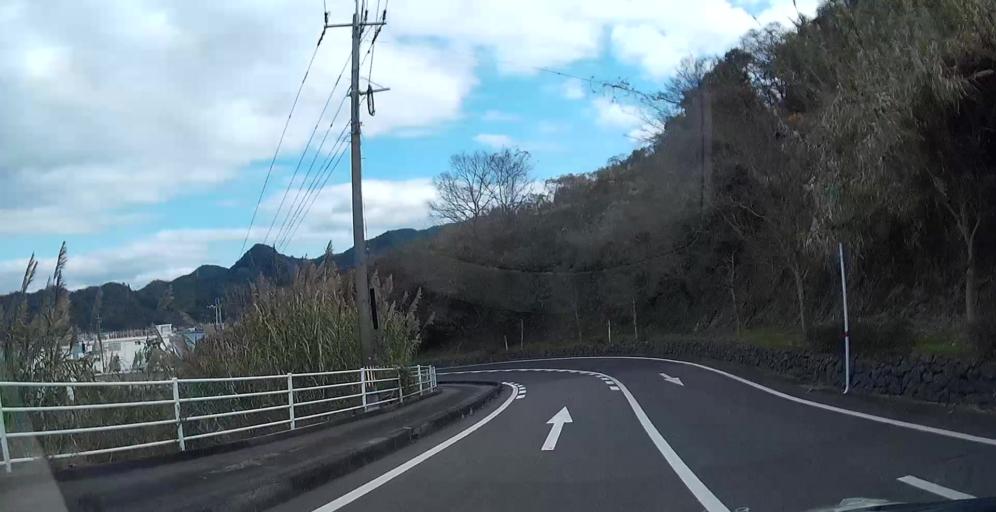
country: JP
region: Kumamoto
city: Minamata
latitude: 32.3271
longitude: 130.4768
